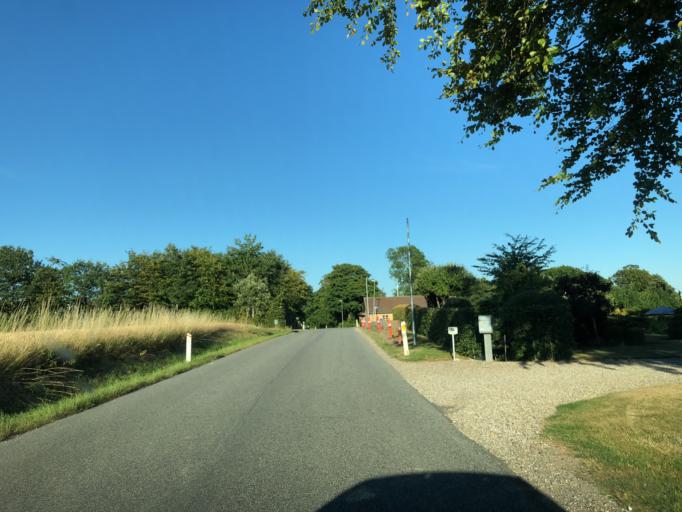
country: DK
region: Central Jutland
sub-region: Horsens Kommune
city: Horsens
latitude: 55.9443
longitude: 9.8651
